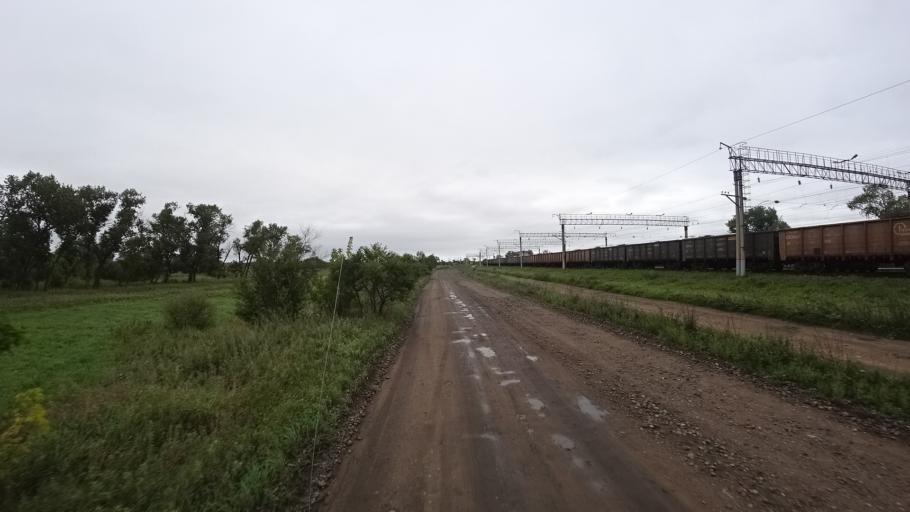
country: RU
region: Primorskiy
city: Chernigovka
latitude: 44.3409
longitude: 132.5340
